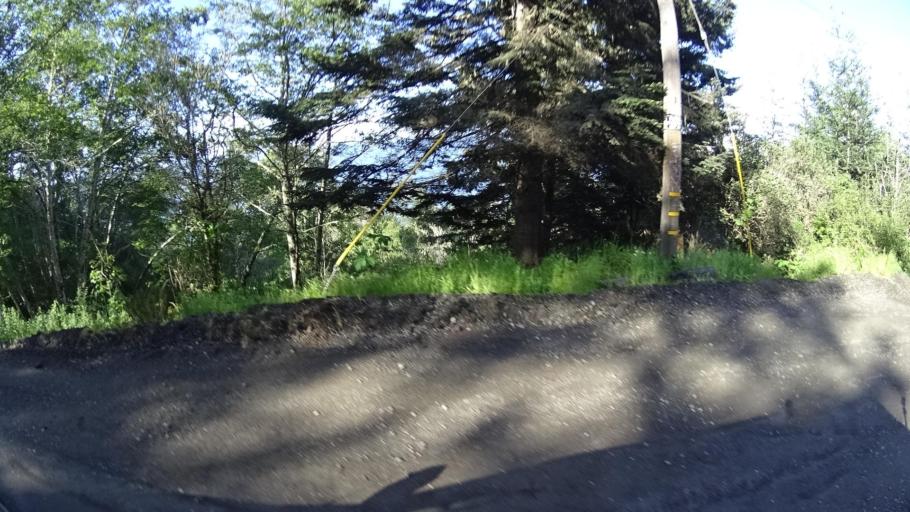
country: US
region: California
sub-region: Humboldt County
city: Westhaven-Moonstone
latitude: 41.0511
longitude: -124.1270
